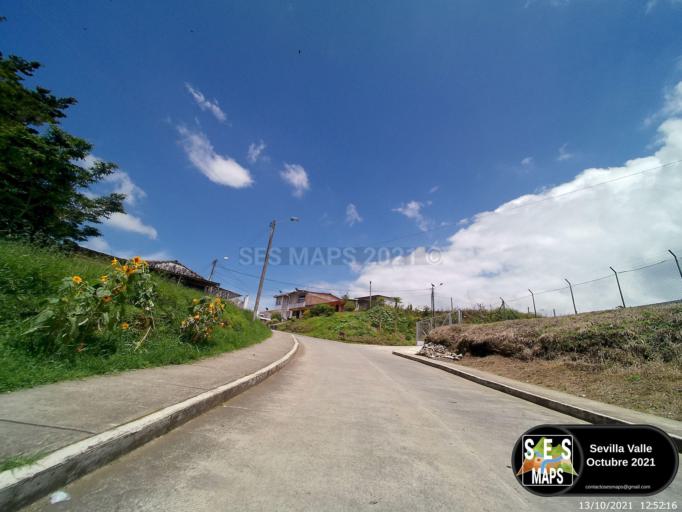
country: CO
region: Valle del Cauca
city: Sevilla
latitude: 4.2705
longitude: -75.9308
